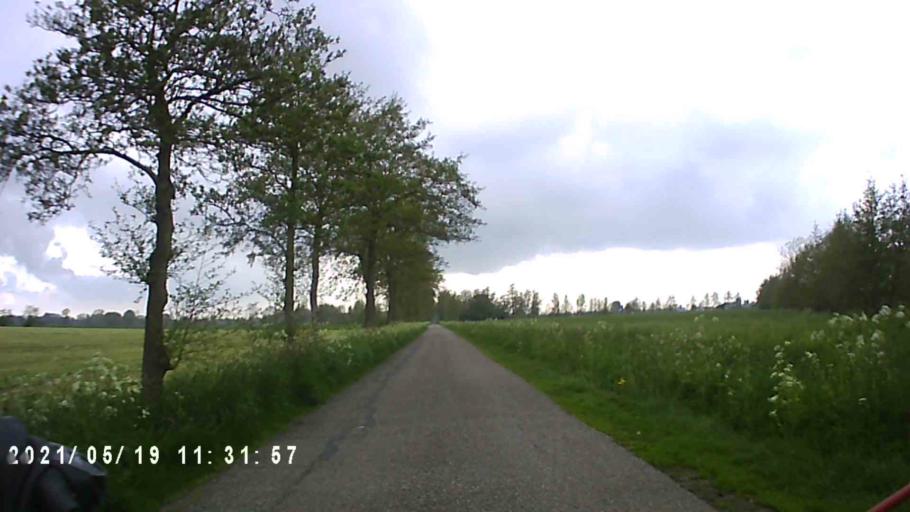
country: NL
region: Friesland
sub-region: Gemeente Kollumerland en Nieuwkruisland
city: Kollum
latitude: 53.2754
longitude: 6.1722
